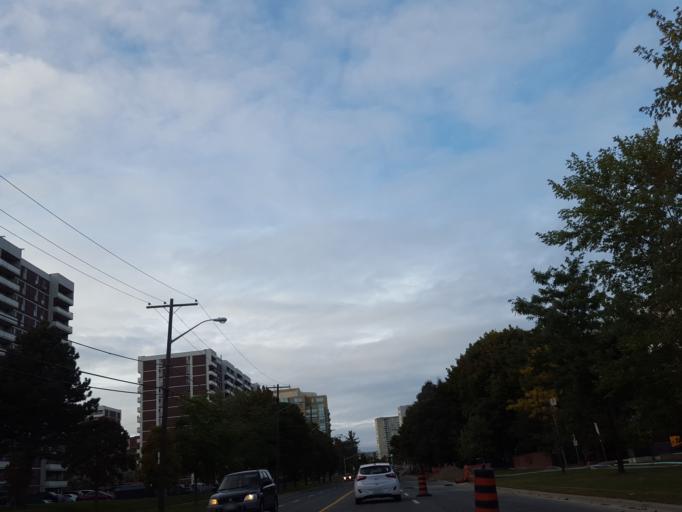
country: CA
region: Ontario
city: Scarborough
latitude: 43.7929
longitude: -79.3142
